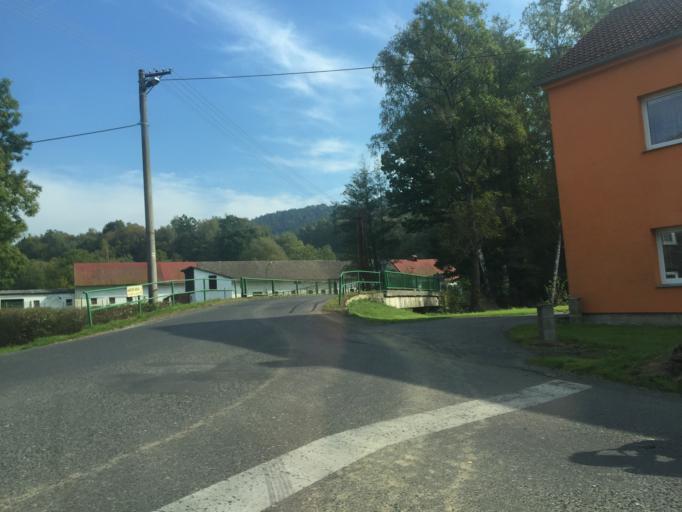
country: CZ
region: Ustecky
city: Ceska Kamenice
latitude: 50.8137
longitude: 14.3511
